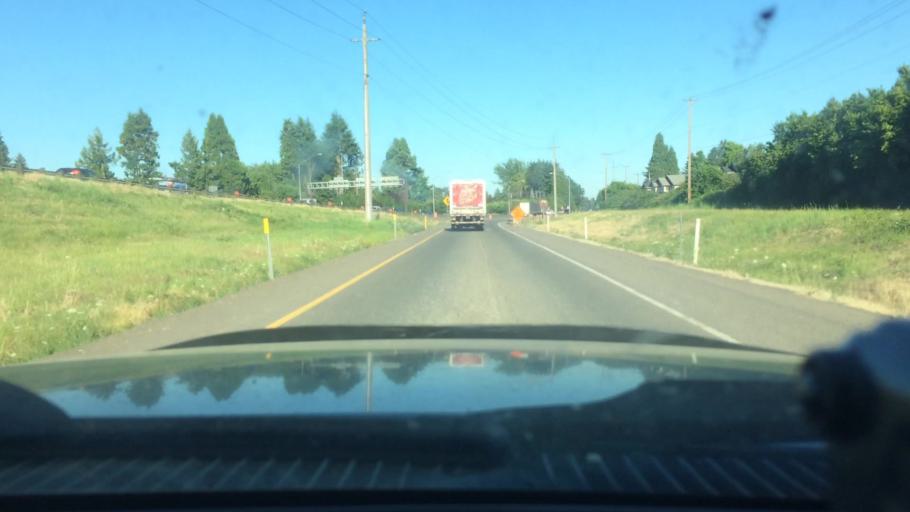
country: US
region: Oregon
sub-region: Lane County
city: Eugene
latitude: 44.0975
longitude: -123.1300
